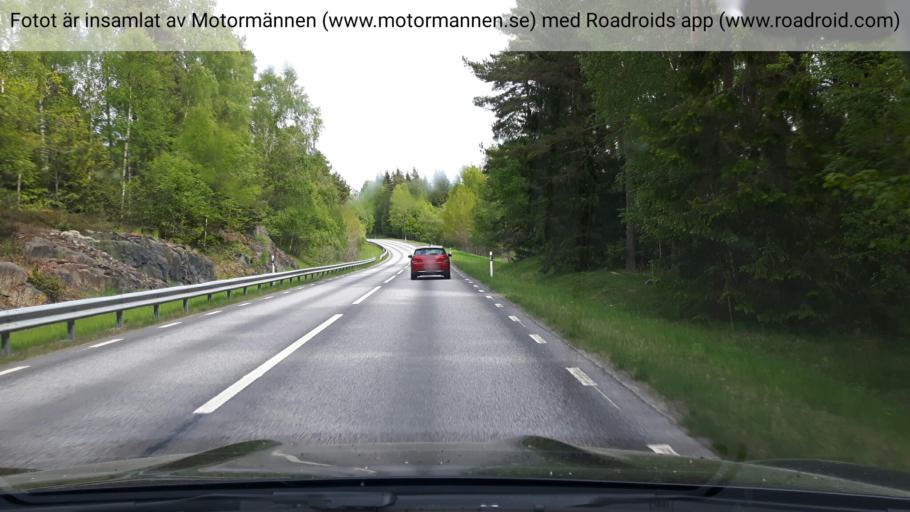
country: SE
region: Stockholm
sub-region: Norrtalje Kommun
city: Norrtalje
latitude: 59.5624
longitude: 18.5831
